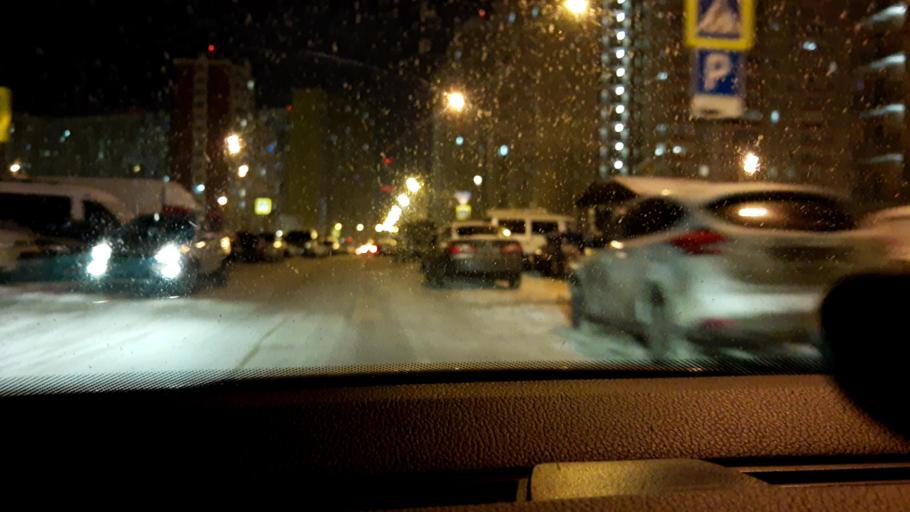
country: RU
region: Moscow
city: Khimki
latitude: 55.8733
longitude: 37.3947
